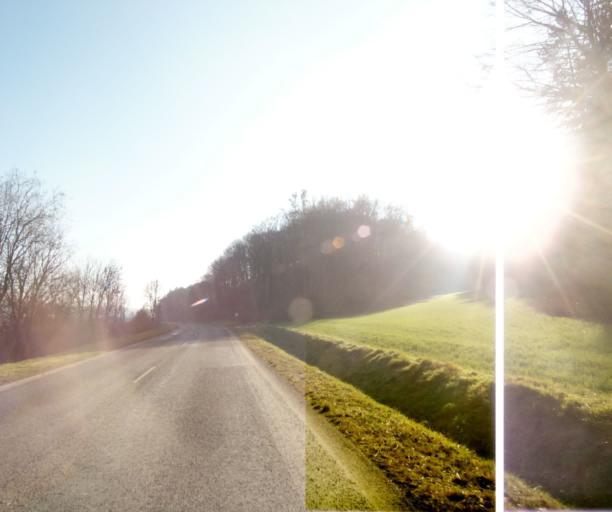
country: FR
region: Champagne-Ardenne
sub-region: Departement de la Haute-Marne
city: Chevillon
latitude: 48.4978
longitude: 5.1201
